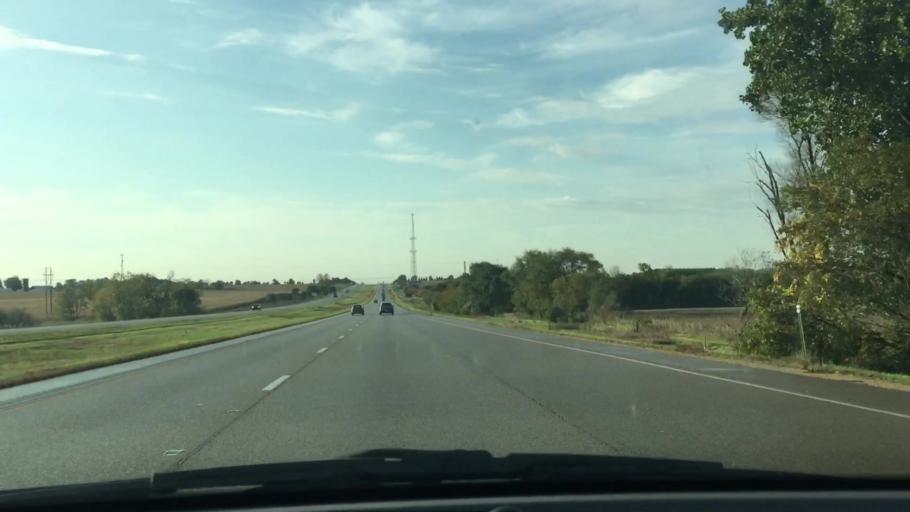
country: US
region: Illinois
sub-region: Ogle County
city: Davis Junction
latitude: 42.1612
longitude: -89.0238
